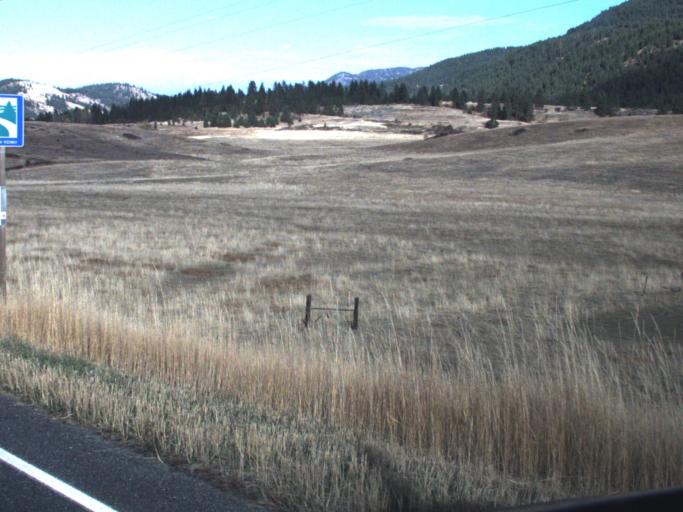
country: US
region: Washington
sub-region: Stevens County
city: Kettle Falls
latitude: 48.4383
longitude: -118.1705
